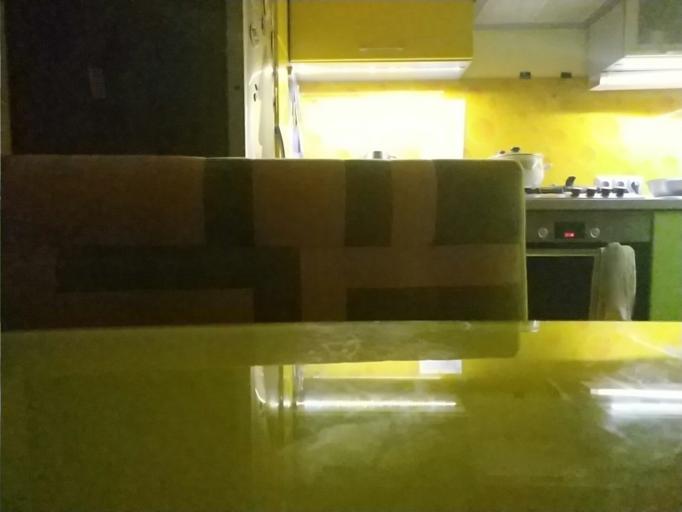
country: RU
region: Republic of Karelia
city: Kalevala
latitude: 65.2785
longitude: 30.7113
